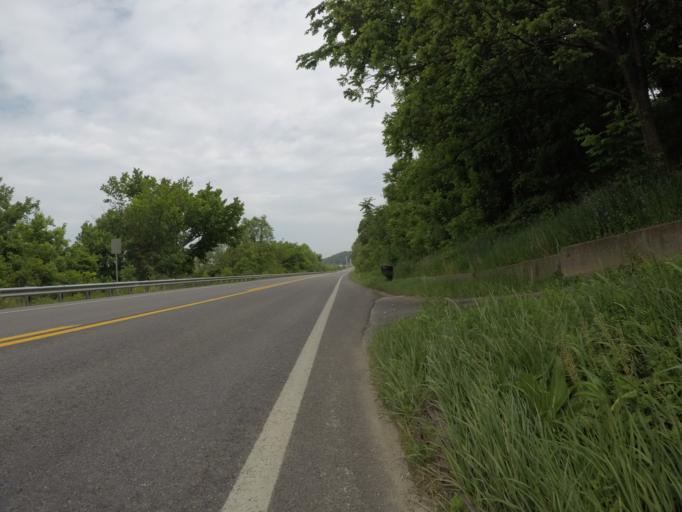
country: US
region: West Virginia
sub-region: Wayne County
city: Kenova
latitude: 38.3634
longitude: -82.5928
